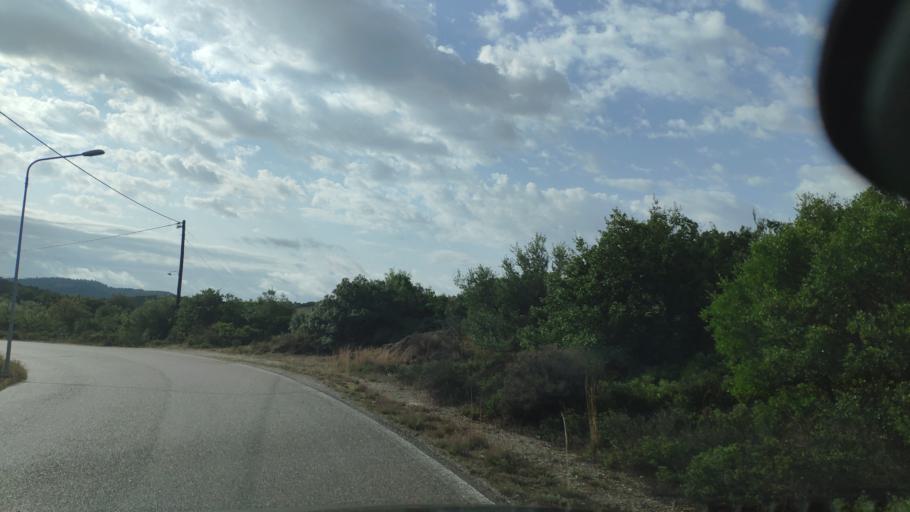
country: GR
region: West Greece
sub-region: Nomos Aitolias kai Akarnanias
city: Sardinia
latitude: 38.8762
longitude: 21.2494
